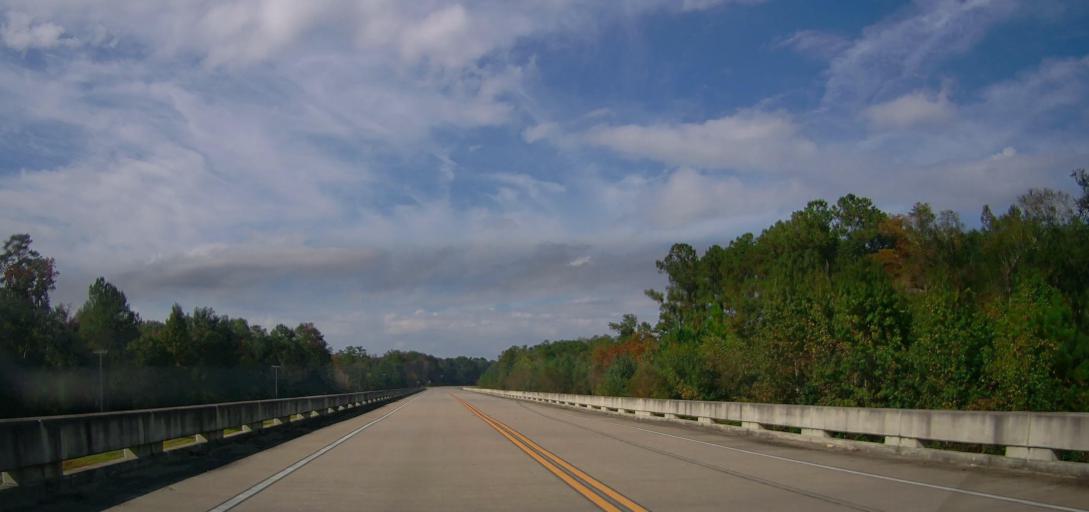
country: US
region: Georgia
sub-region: Thomas County
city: Thomasville
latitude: 30.9129
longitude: -84.0087
